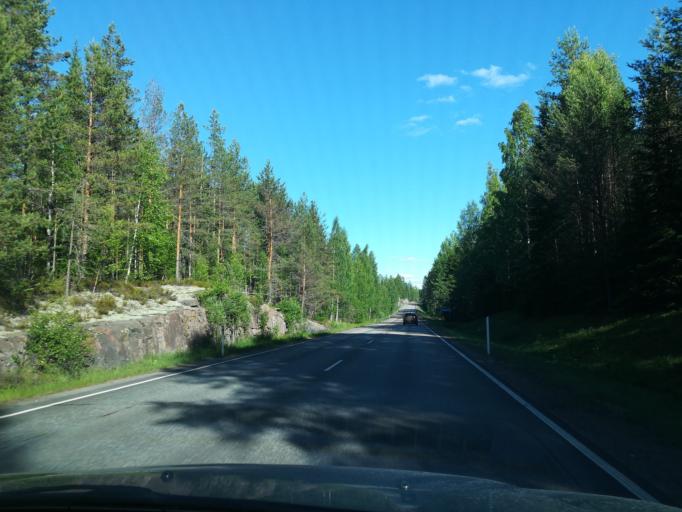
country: FI
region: South Karelia
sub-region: Imatra
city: Ruokolahti
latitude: 61.3648
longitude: 28.6904
